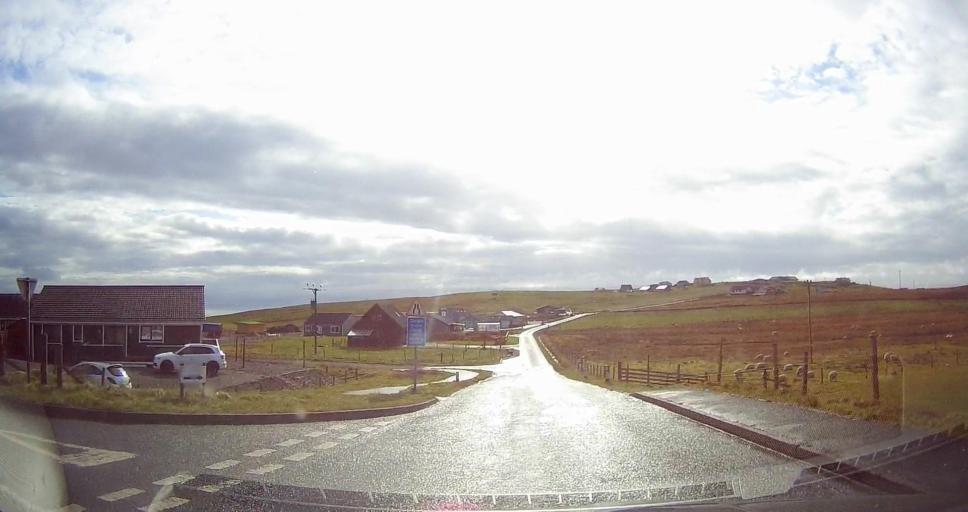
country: GB
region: Scotland
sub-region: Shetland Islands
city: Sandwick
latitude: 60.0604
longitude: -1.2216
